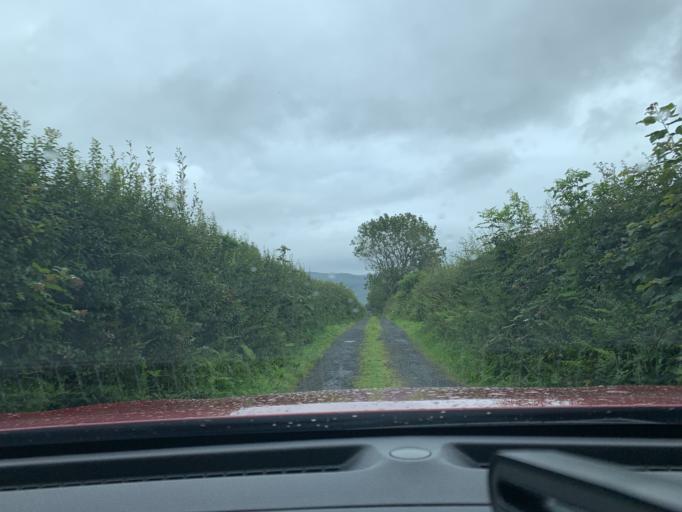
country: IE
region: Connaught
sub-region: Sligo
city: Sligo
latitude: 54.3056
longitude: -8.4454
